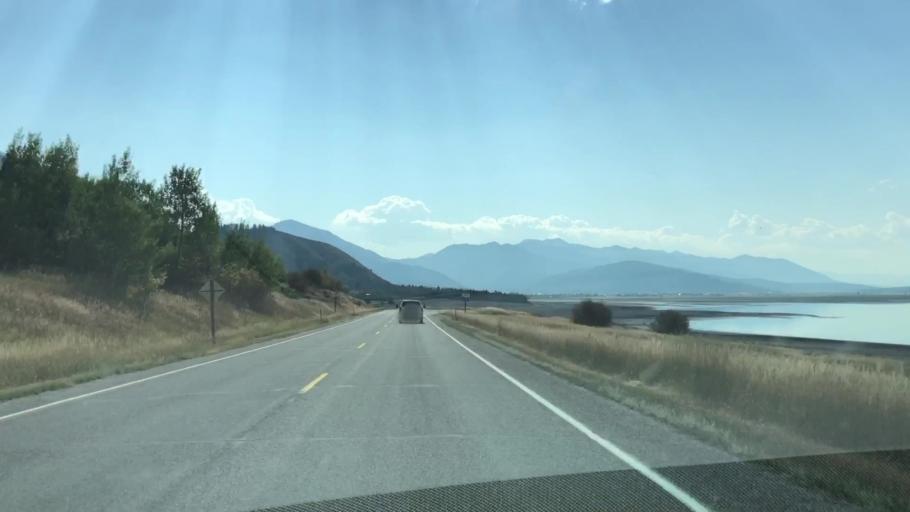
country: US
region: Wyoming
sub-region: Teton County
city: Hoback
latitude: 43.2214
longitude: -111.0737
